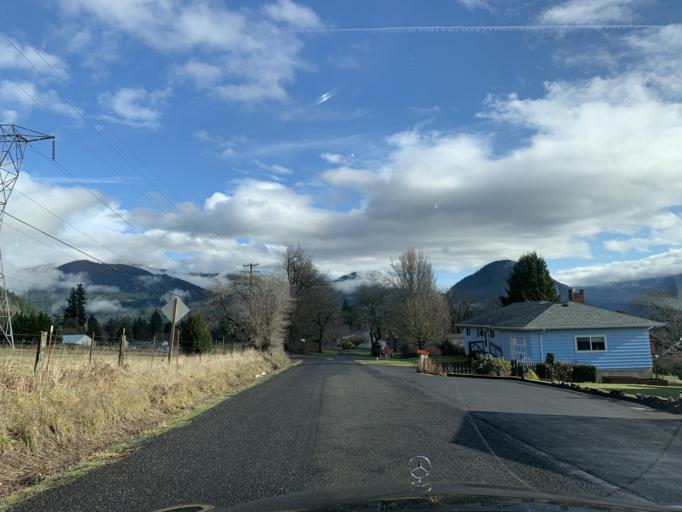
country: US
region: Washington
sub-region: Skamania County
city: Carson
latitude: 45.7222
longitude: -121.8109
